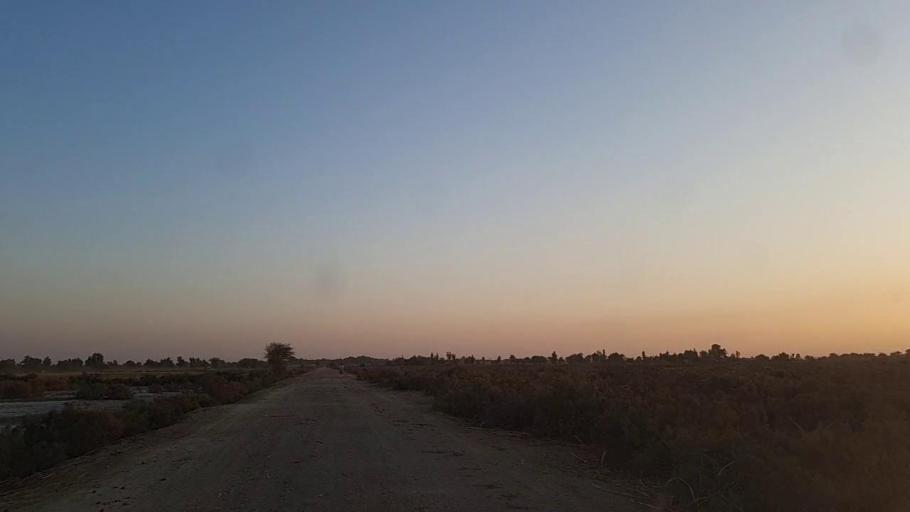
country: PK
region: Sindh
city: Samaro
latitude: 25.3176
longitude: 69.3691
